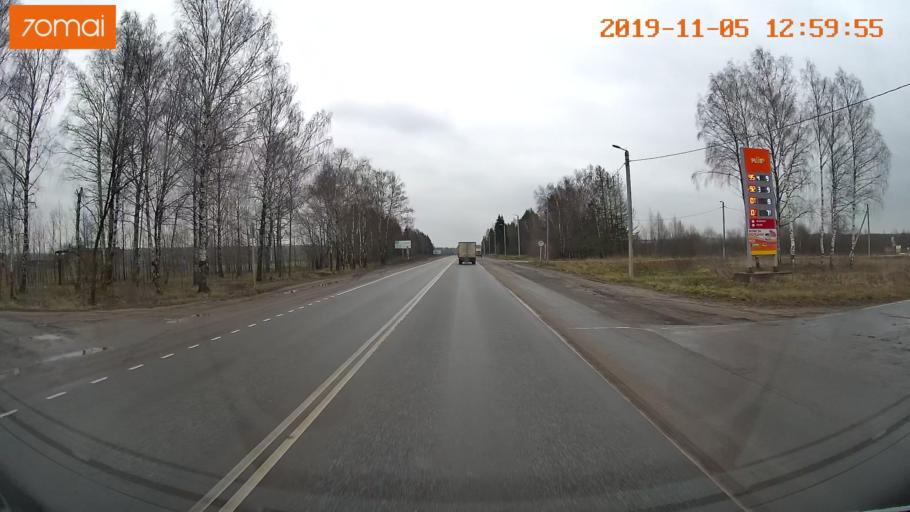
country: RU
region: Ivanovo
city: Kokhma
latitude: 56.9160
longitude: 41.1375
